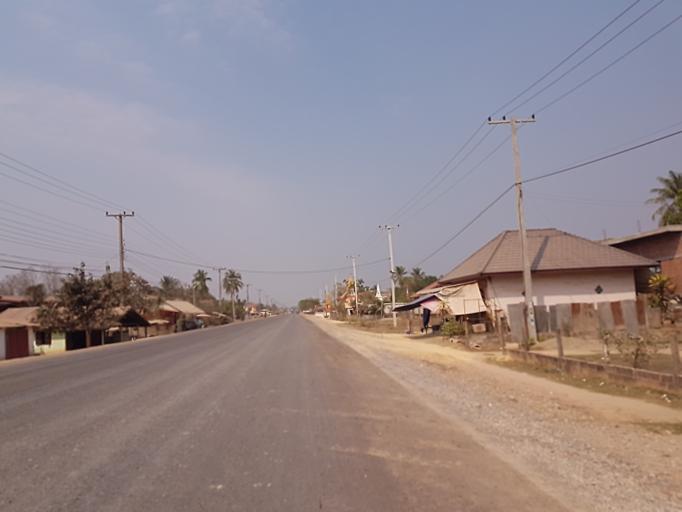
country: TH
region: Nong Khai
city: Nong Khai
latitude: 17.9157
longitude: 102.7654
